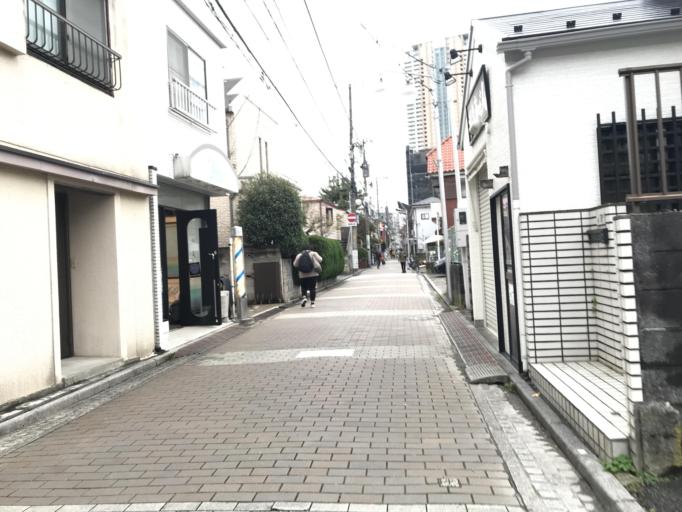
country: JP
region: Chiba
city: Matsudo
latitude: 35.7330
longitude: 139.9072
